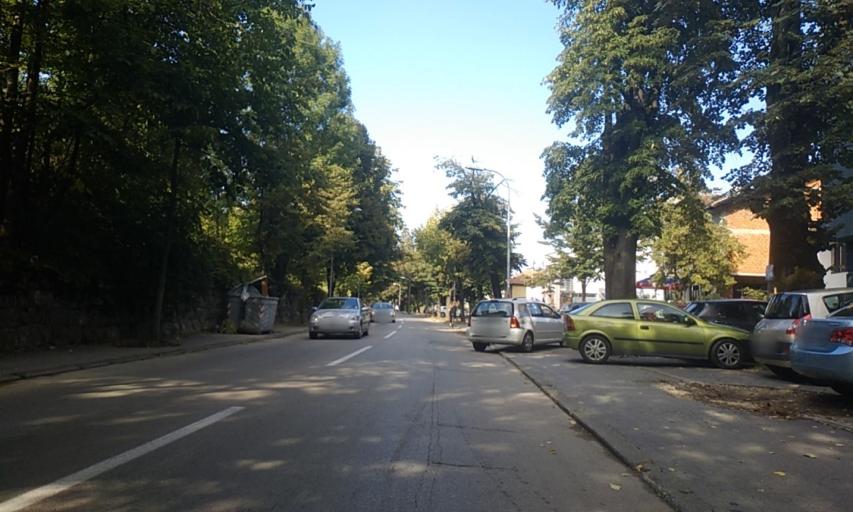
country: BA
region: Republika Srpska
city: Hiseti
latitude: 44.7575
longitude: 17.1782
